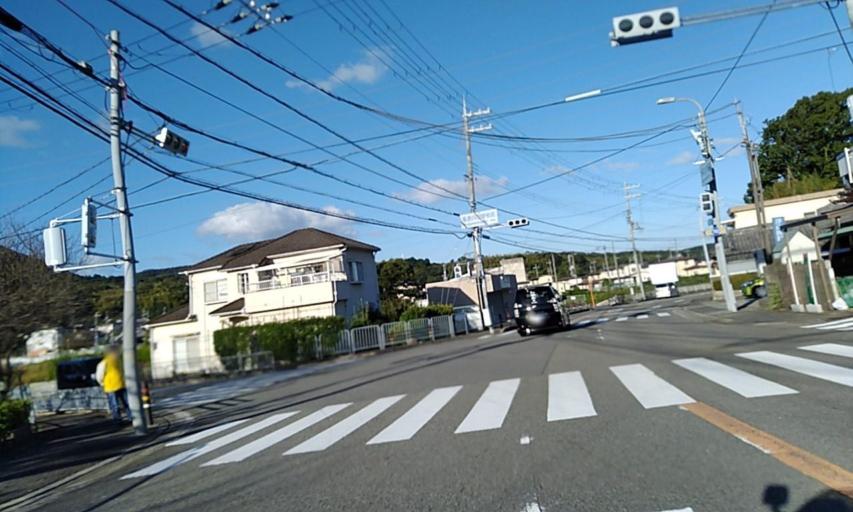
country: JP
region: Wakayama
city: Wakayama-shi
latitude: 34.3157
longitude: 135.1269
